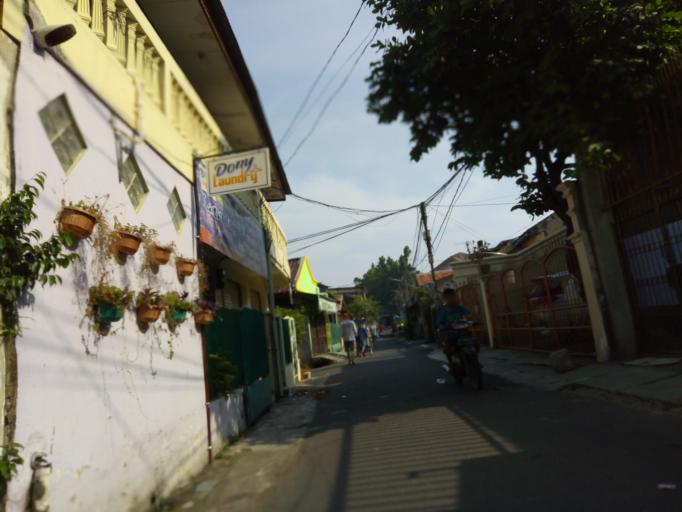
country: ID
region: Jakarta Raya
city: Jakarta
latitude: -6.2098
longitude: 106.8391
